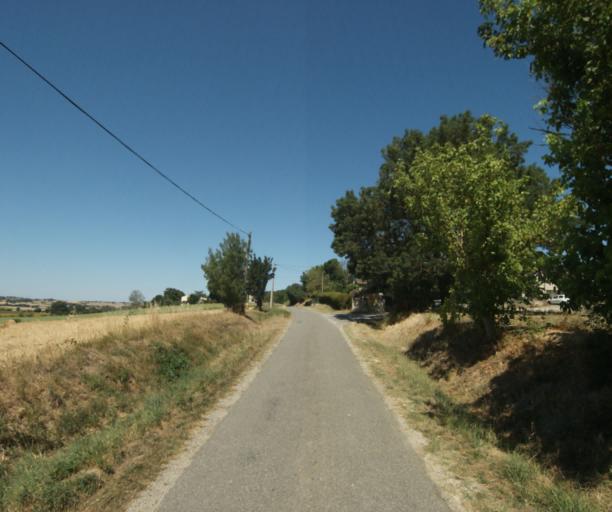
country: FR
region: Midi-Pyrenees
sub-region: Departement de la Haute-Garonne
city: Saint-Felix-Lauragais
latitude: 43.4952
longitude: 1.9284
